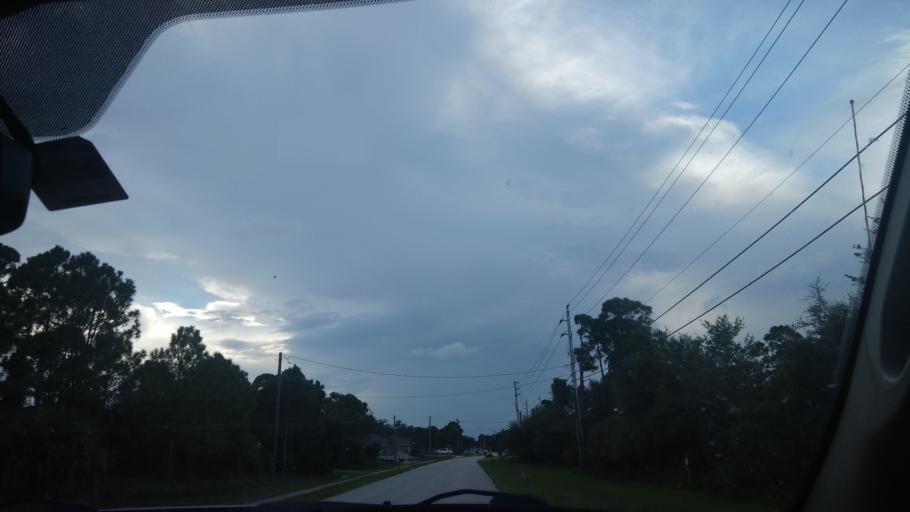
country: US
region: Florida
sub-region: Indian River County
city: Sebastian
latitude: 27.7778
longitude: -80.4732
